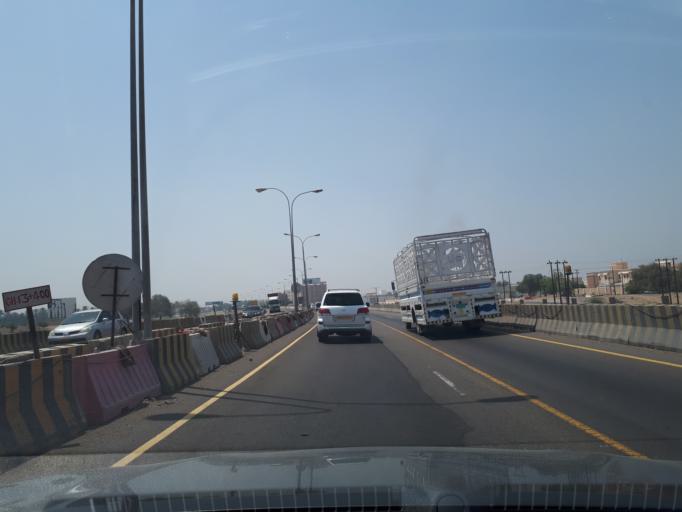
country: OM
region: Al Batinah
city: Al Sohar
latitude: 24.3877
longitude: 56.6997
